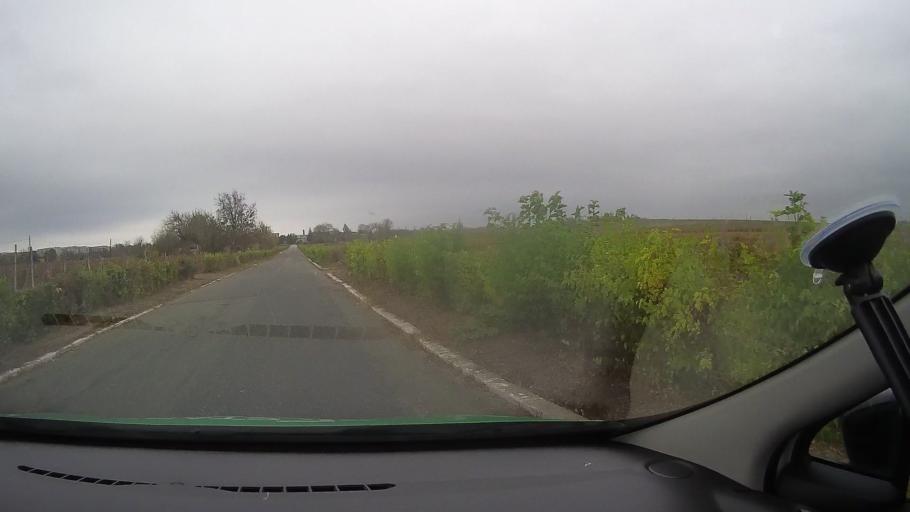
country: RO
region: Constanta
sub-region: Oras Murfatlar
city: Murfatlar
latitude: 44.1725
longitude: 28.4226
